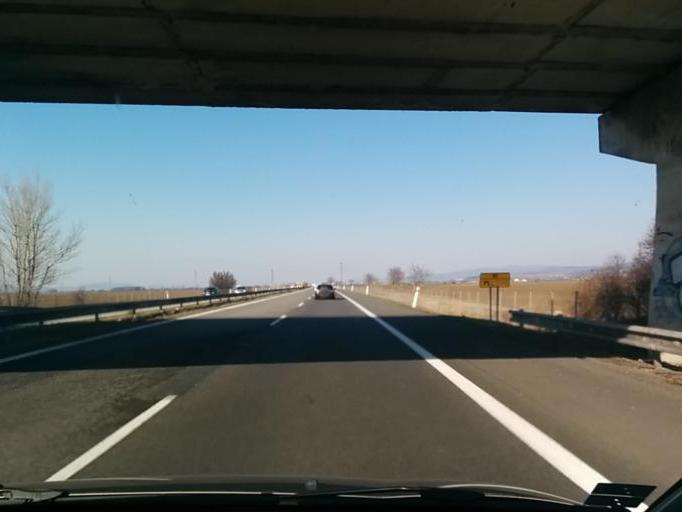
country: SK
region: Trnavsky
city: Leopoldov
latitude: 48.5207
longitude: 17.7770
